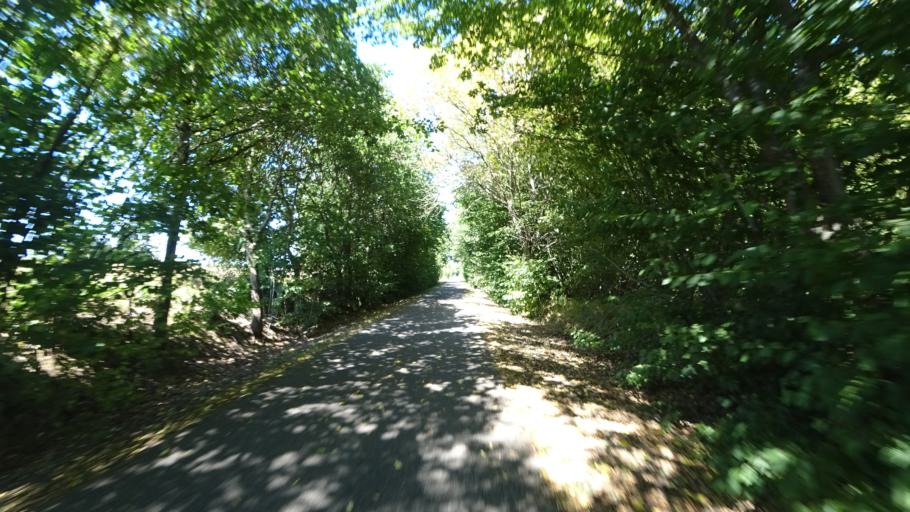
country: DE
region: Rheinland-Pfalz
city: Keidelheim
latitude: 49.9972
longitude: 7.5008
